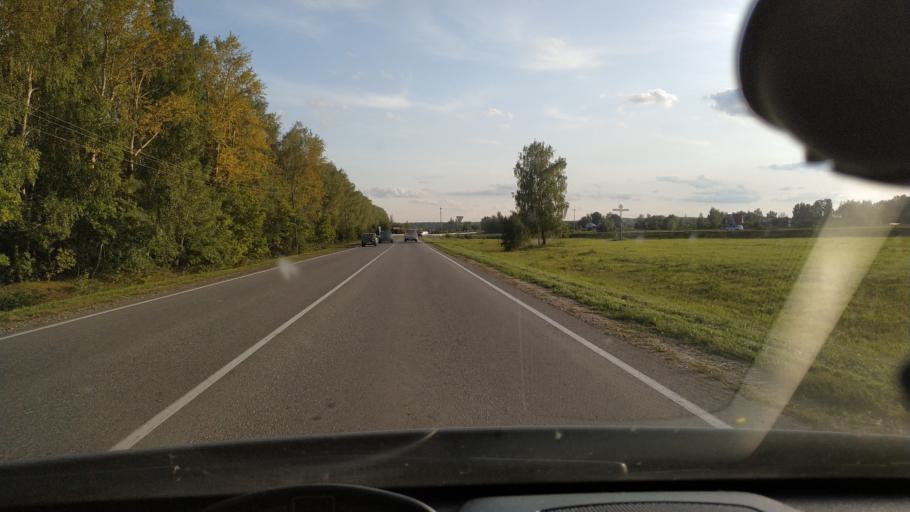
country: RU
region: Rjazan
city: Rybnoye
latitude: 54.8212
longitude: 39.6095
